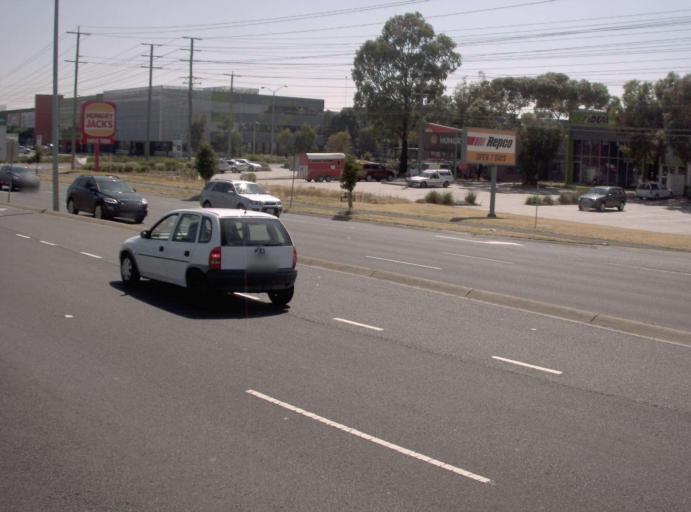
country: AU
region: Victoria
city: Highett
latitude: -37.9508
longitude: 145.0772
